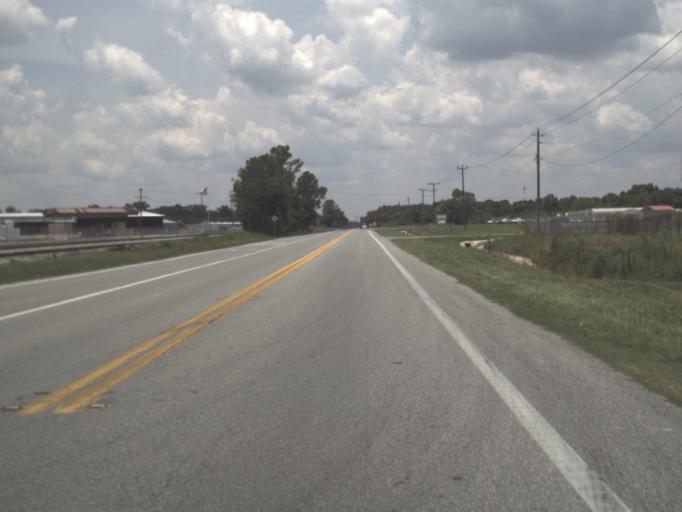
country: US
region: Florida
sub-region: Columbia County
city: Watertown
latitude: 30.1687
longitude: -82.5785
